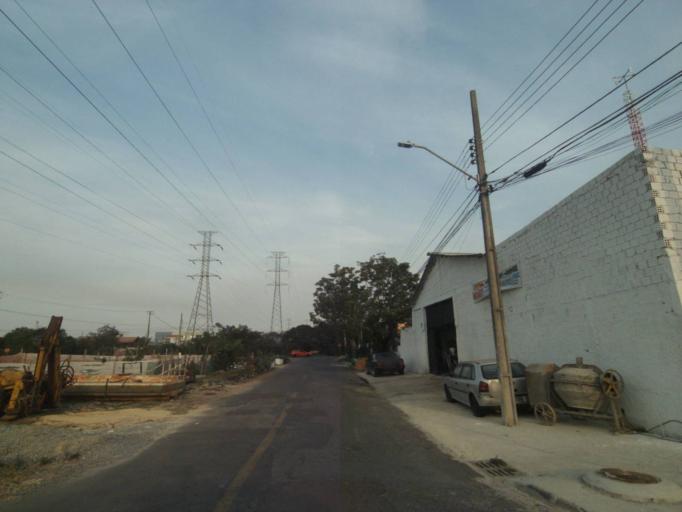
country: BR
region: Parana
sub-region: Pinhais
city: Pinhais
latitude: -25.4845
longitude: -49.2013
